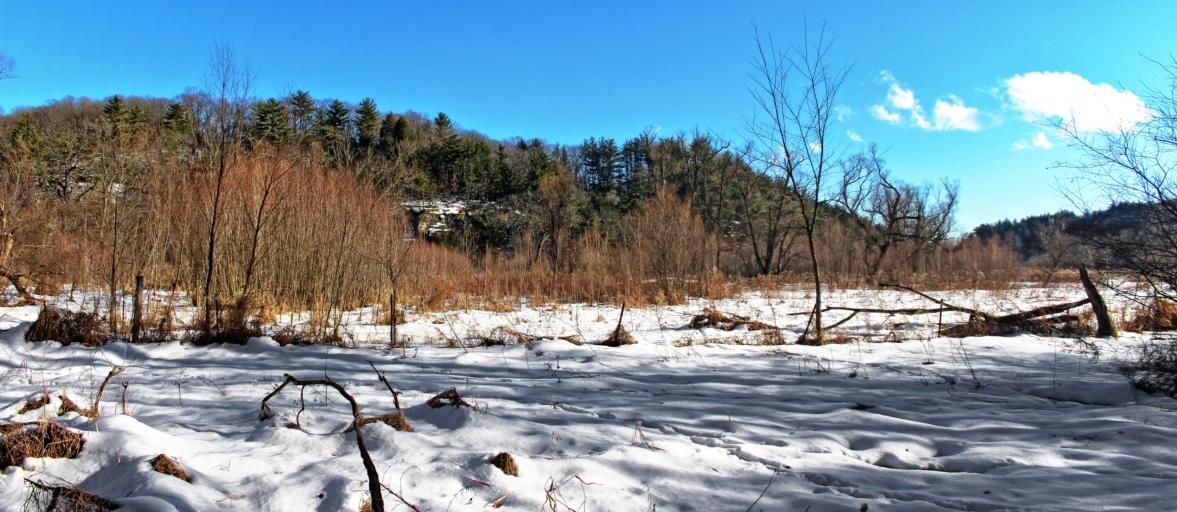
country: US
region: Wisconsin
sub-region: Sauk County
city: Reedsburg
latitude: 43.3580
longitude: -89.9828
